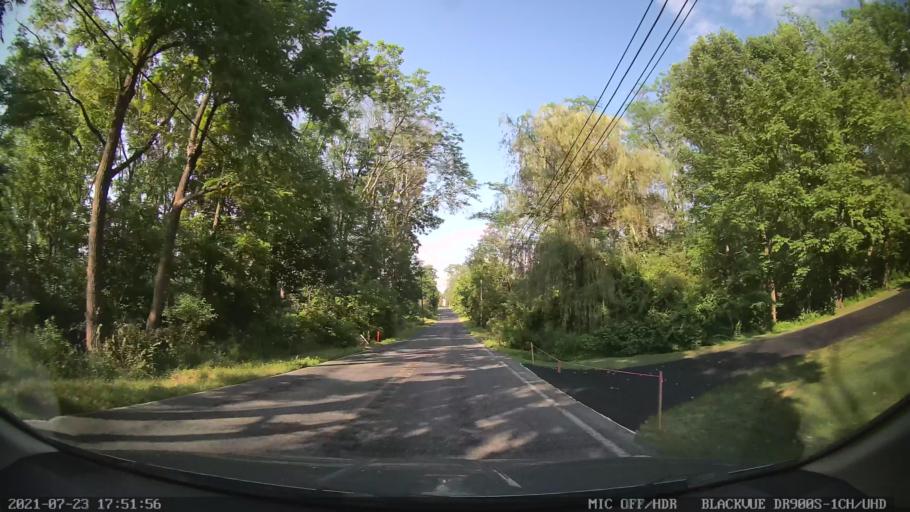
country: US
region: Pennsylvania
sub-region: Lehigh County
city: Alburtis
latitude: 40.4989
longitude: -75.5828
